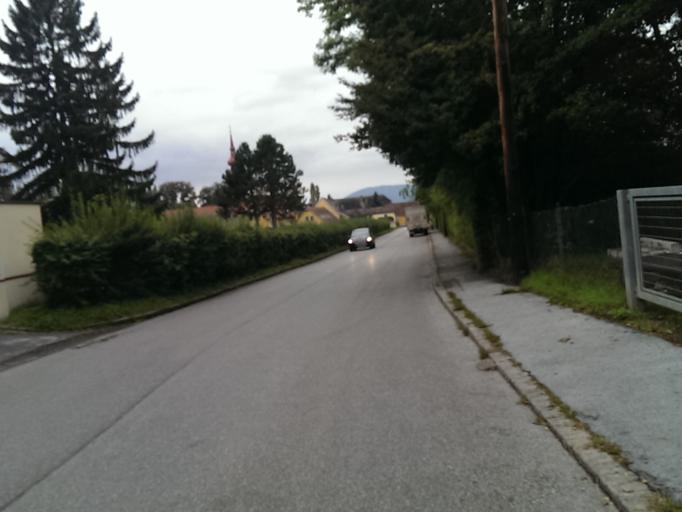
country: AT
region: Styria
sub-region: Graz Stadt
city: Graz
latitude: 47.0561
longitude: 15.4783
